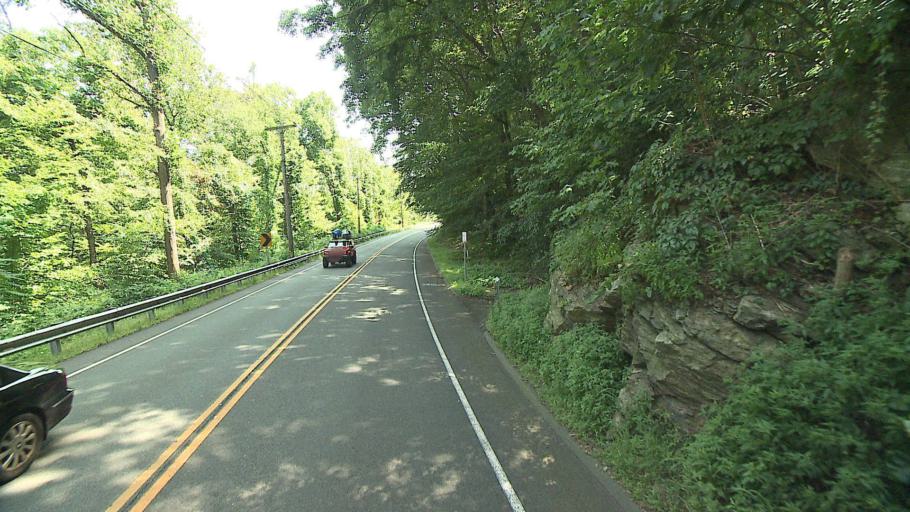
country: US
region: Connecticut
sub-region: Fairfield County
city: Shelton
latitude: 41.3367
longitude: -73.1241
